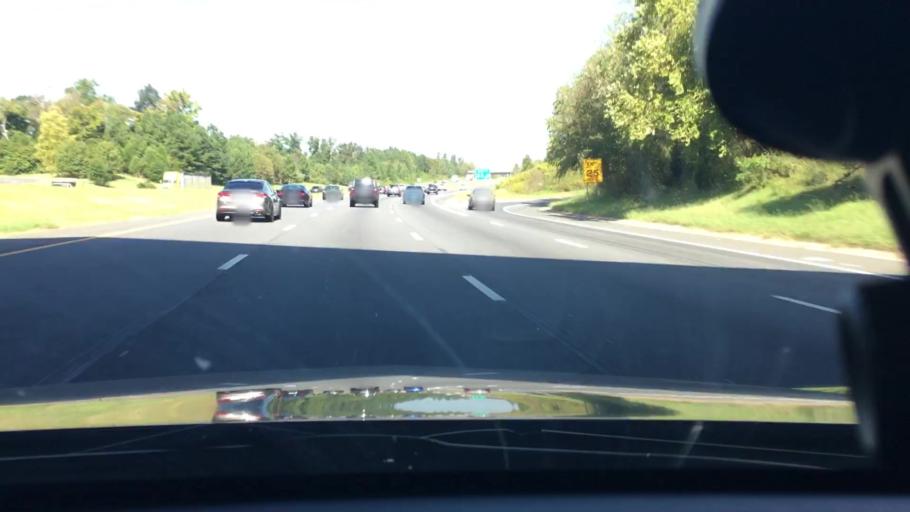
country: US
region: North Carolina
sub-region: Cabarrus County
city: Harrisburg
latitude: 35.3125
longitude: -80.7077
